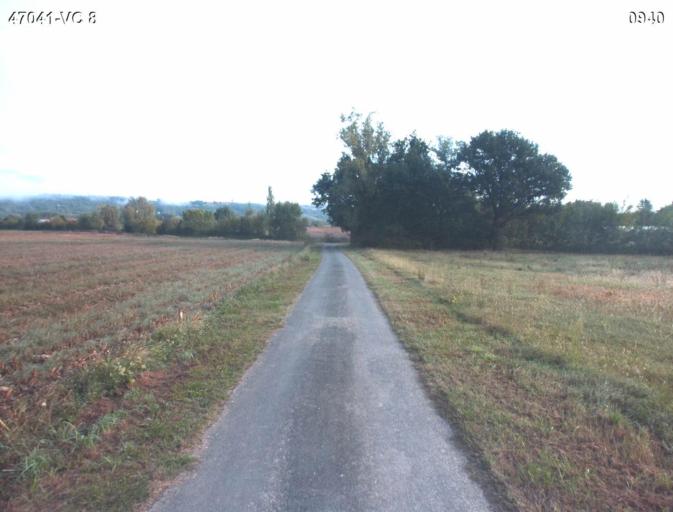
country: FR
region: Aquitaine
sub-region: Departement du Lot-et-Garonne
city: Port-Sainte-Marie
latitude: 44.2218
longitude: 0.4343
